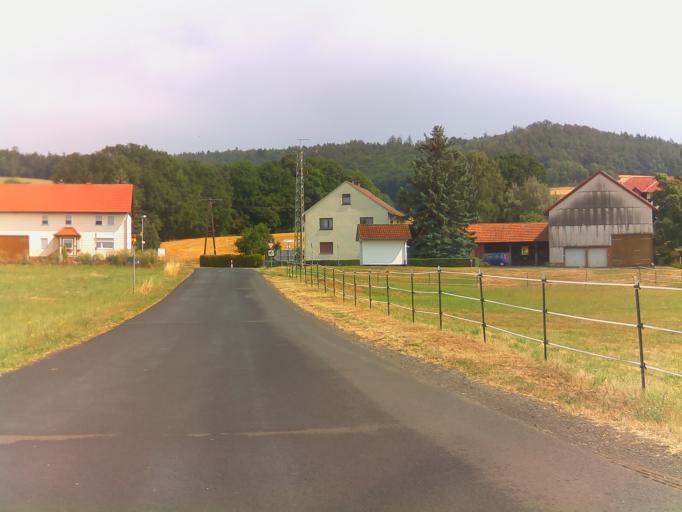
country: DE
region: Hesse
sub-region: Regierungsbezirk Kassel
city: Niederaula
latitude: 50.7706
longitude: 9.5942
